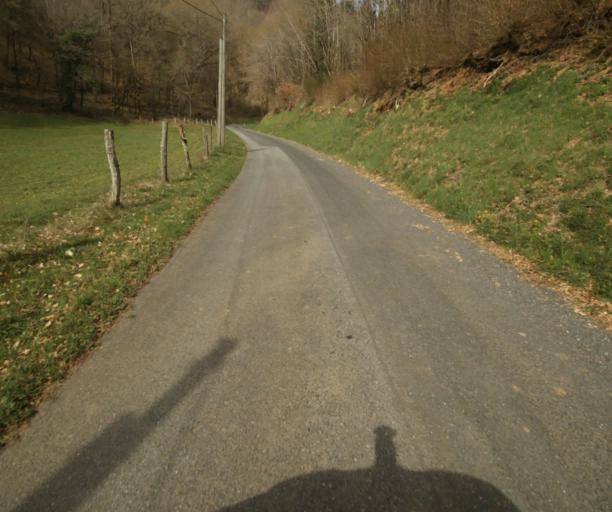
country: FR
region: Limousin
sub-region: Departement de la Correze
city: Naves
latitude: 45.3500
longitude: 1.8135
